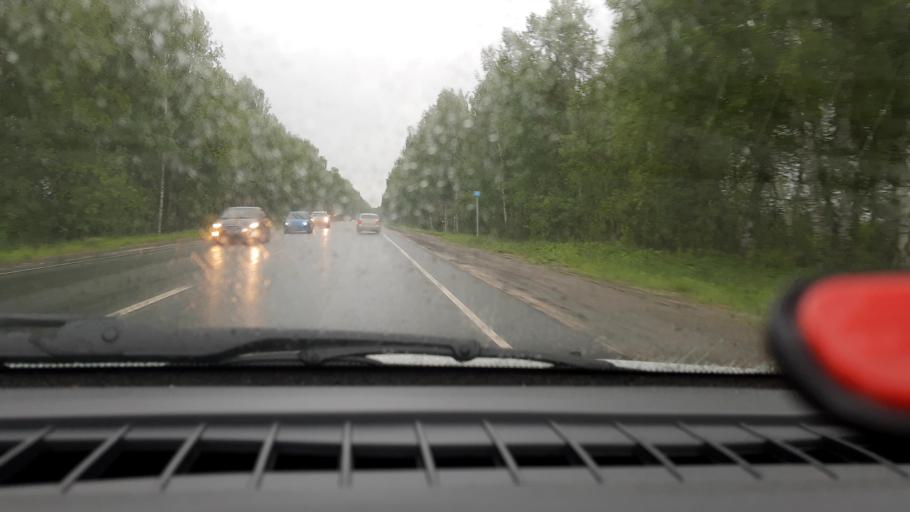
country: RU
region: Nizjnij Novgorod
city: Linda
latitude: 56.5478
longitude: 44.0202
